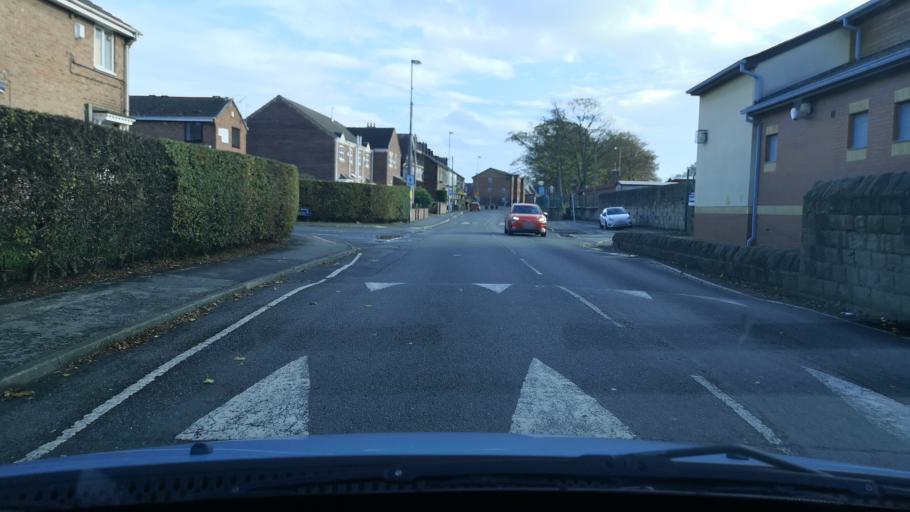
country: GB
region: England
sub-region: City and Borough of Wakefield
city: Crofton
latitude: 53.6575
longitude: -1.4298
